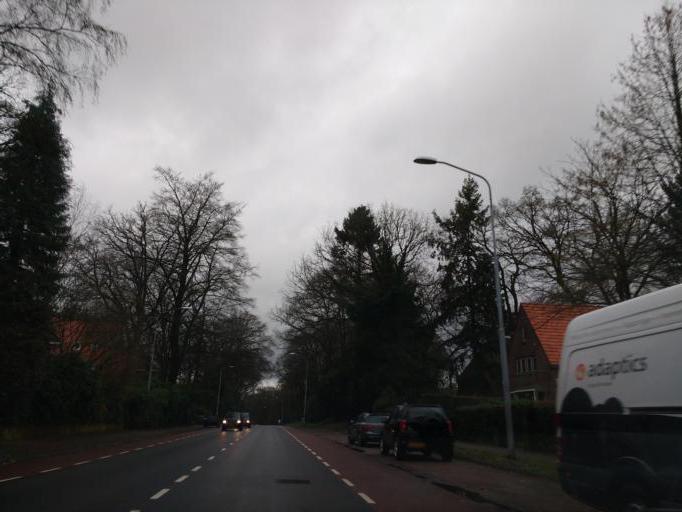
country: NL
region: Gelderland
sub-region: Gemeente Groesbeek
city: Berg en Dal
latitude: 51.8289
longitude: 5.9015
